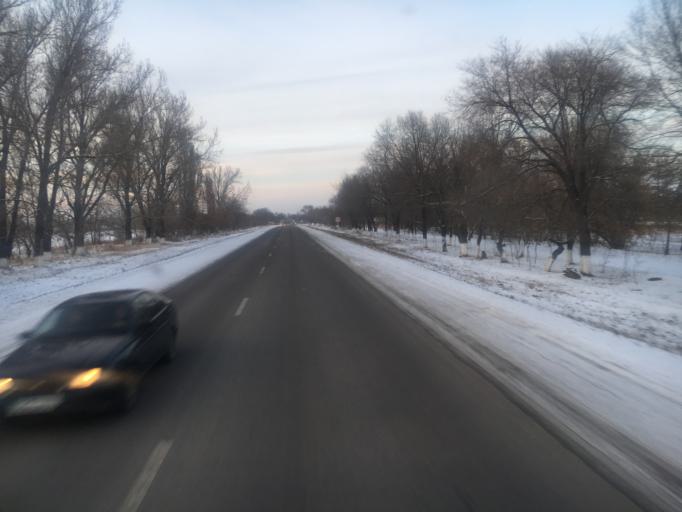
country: KZ
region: Almaty Oblysy
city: Burunday
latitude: 43.3609
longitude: 76.6436
